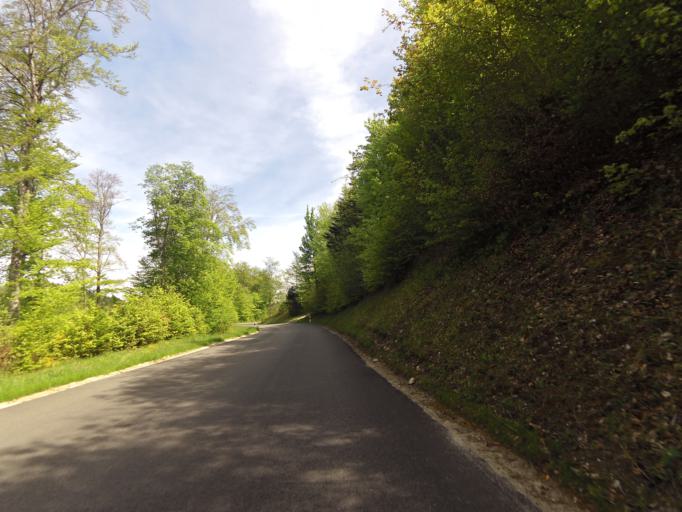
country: CH
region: Vaud
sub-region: Nyon District
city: Arzier
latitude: 46.4652
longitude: 6.2230
